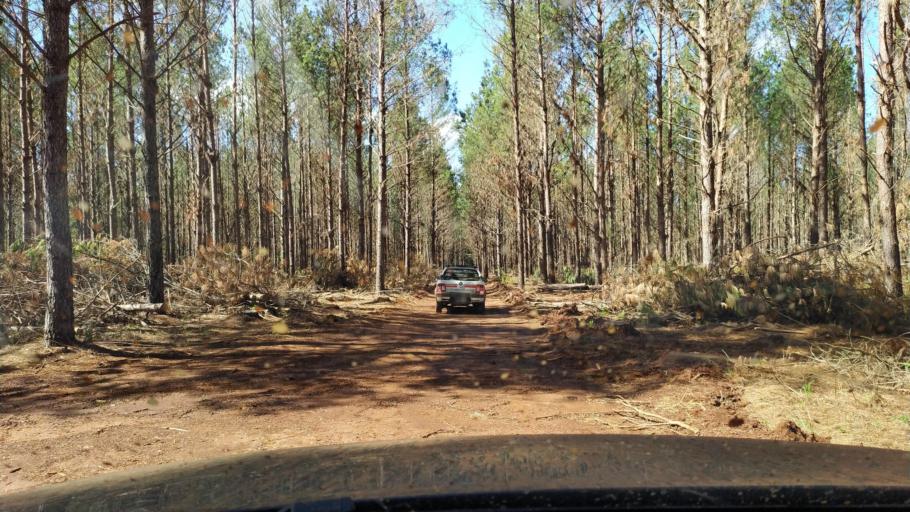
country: AR
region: Corrientes
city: Santo Tome
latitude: -28.4104
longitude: -56.0121
